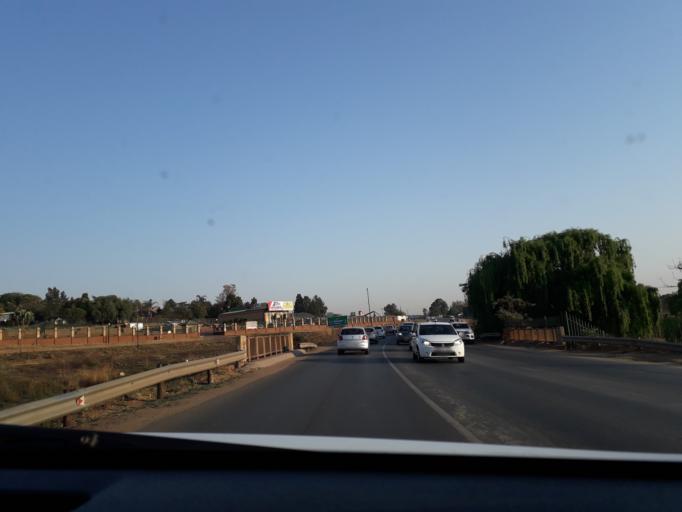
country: ZA
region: Gauteng
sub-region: Ekurhuleni Metropolitan Municipality
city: Tembisa
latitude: -26.0790
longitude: 28.2854
